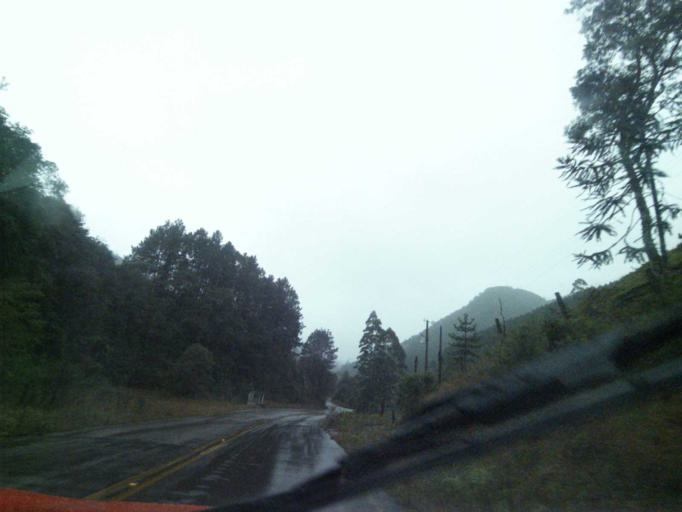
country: BR
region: Santa Catarina
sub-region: Anitapolis
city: Anitapolis
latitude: -27.8031
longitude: -49.0463
